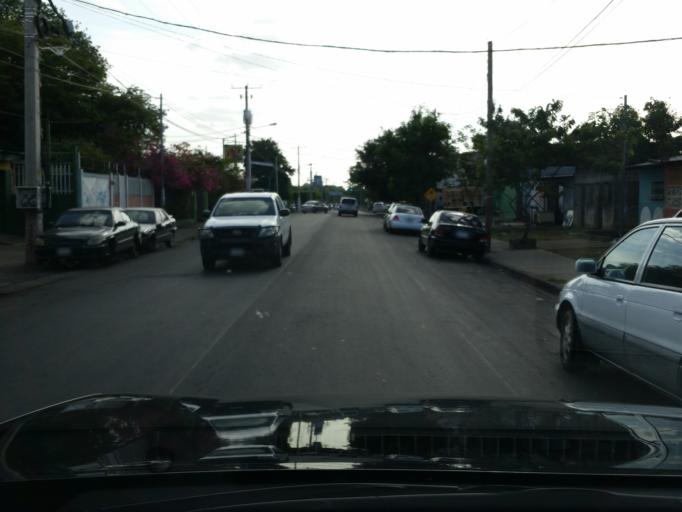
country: NI
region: Managua
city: Managua
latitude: 12.1410
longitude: -86.2404
